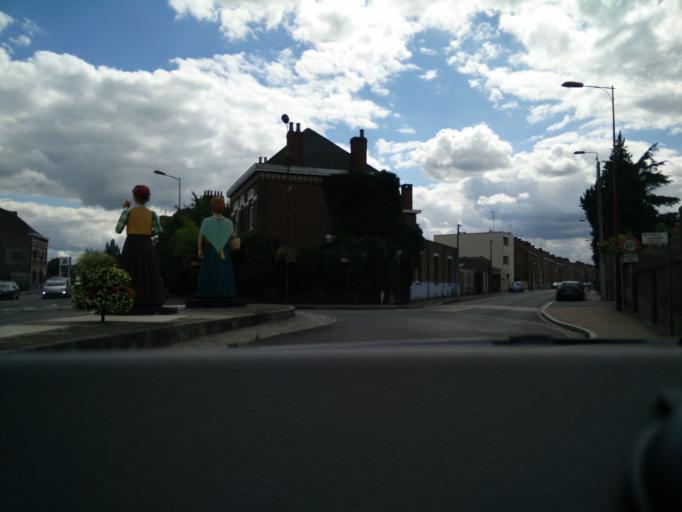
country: FR
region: Nord-Pas-de-Calais
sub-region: Departement du Nord
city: Hazebrouck
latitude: 50.7319
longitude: 2.5439
